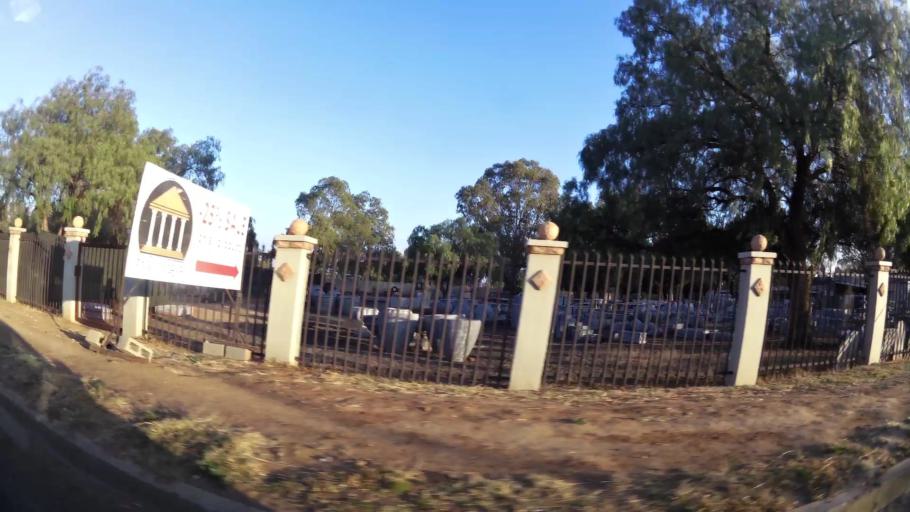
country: ZA
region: Orange Free State
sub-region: Mangaung Metropolitan Municipality
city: Bloemfontein
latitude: -29.0964
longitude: 26.1469
